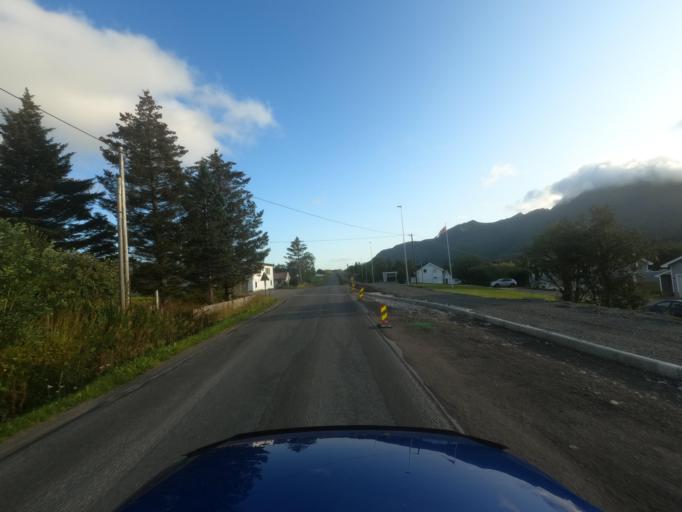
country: NO
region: Nordland
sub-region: Vestvagoy
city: Gravdal
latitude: 68.0994
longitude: 13.5466
